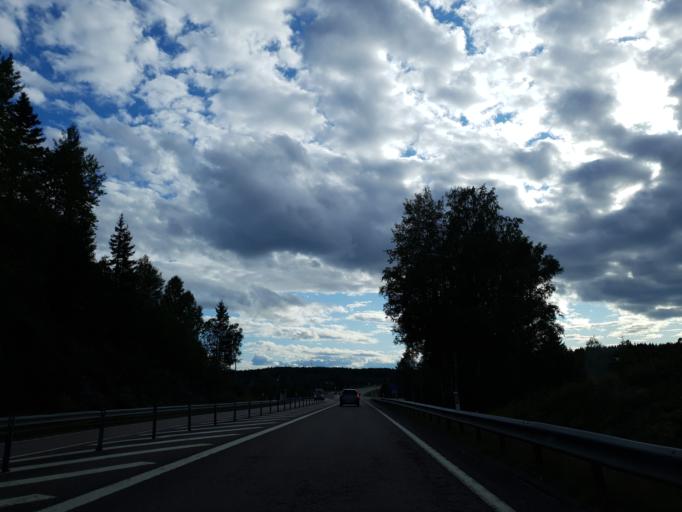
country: SE
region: Vaesternorrland
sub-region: Haernoesands Kommun
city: Haernoesand
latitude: 62.5896
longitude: 17.7906
